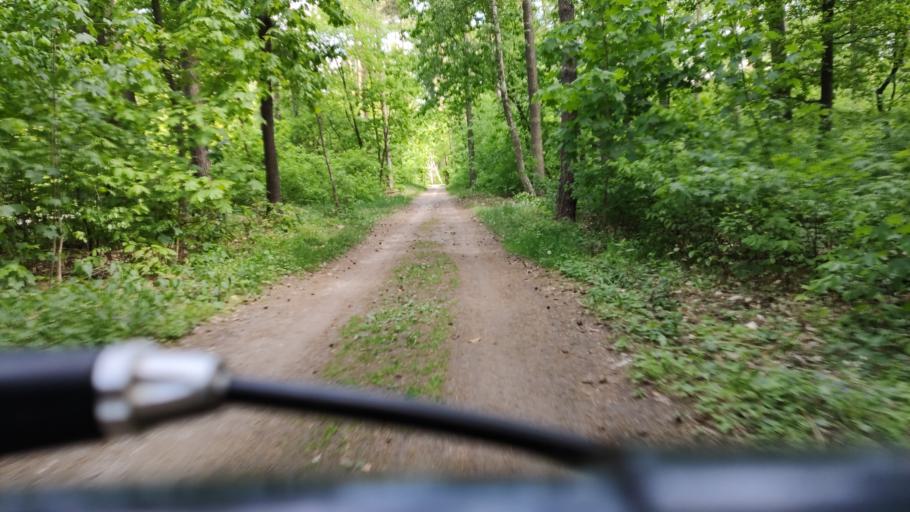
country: PL
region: Kujawsko-Pomorskie
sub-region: Wloclawek
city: Wloclawek
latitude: 52.6376
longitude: 19.1071
